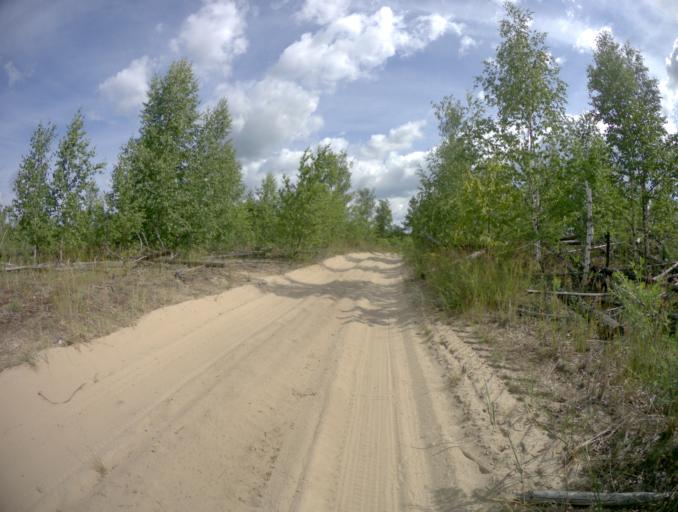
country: RU
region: Ivanovo
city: Talitsy
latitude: 56.5350
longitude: 42.4409
